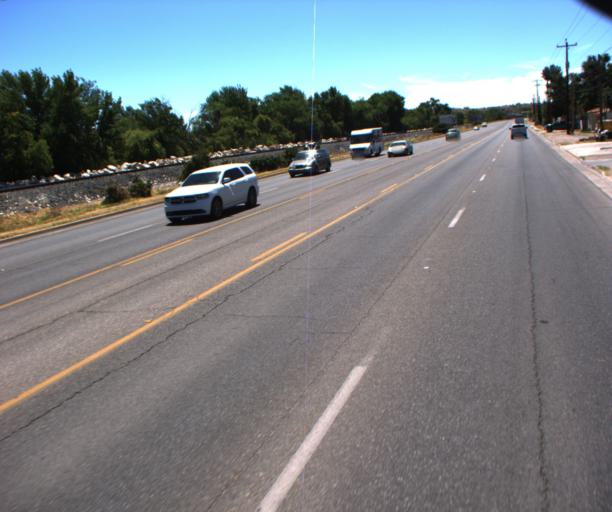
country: US
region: Arizona
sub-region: Santa Cruz County
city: Nogales
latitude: 31.3748
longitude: -110.9363
